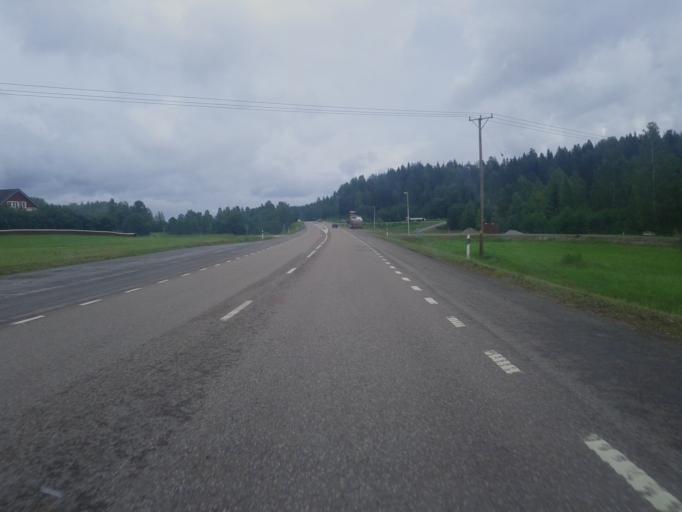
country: SE
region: Vaesternorrland
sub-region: Sundsvalls Kommun
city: Vi
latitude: 62.3808
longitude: 17.1582
